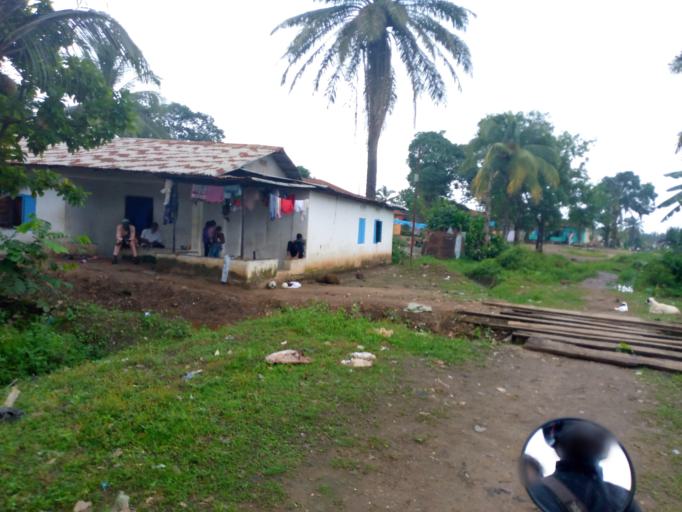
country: SL
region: Eastern Province
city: Kenema
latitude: 7.8646
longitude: -11.1929
